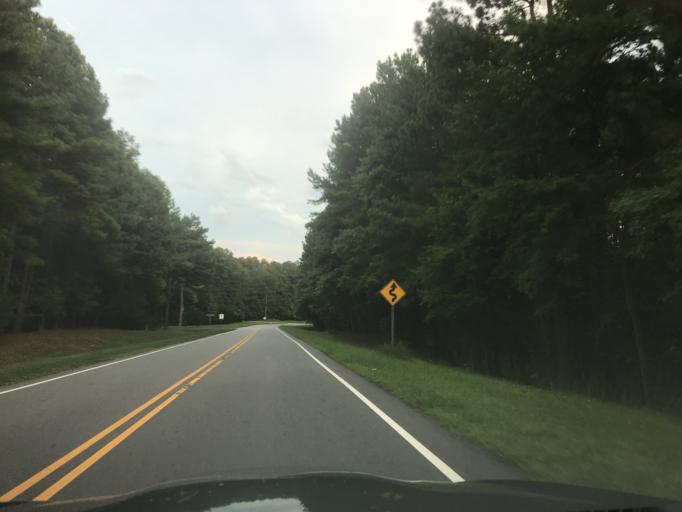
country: US
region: North Carolina
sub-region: Wake County
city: Wake Forest
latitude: 35.9354
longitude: -78.6089
